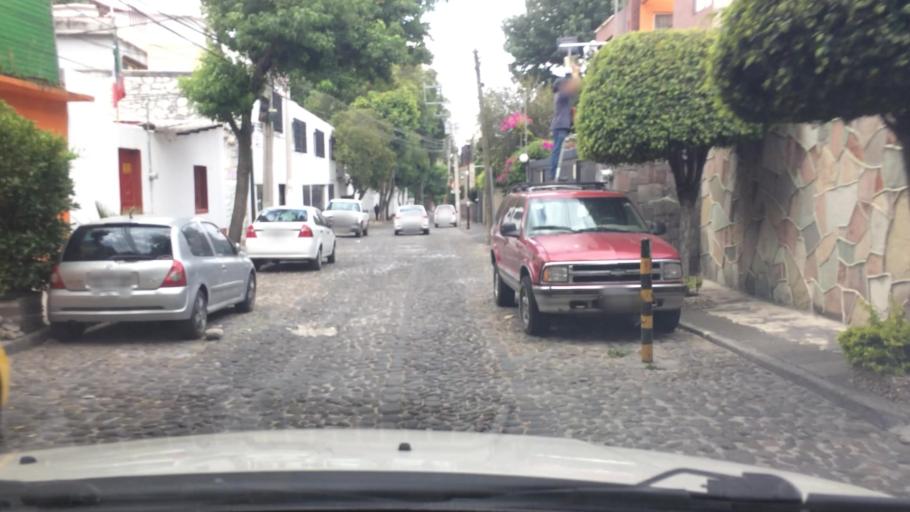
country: MX
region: Mexico City
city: Alvaro Obregon
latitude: 19.3554
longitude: -99.1956
